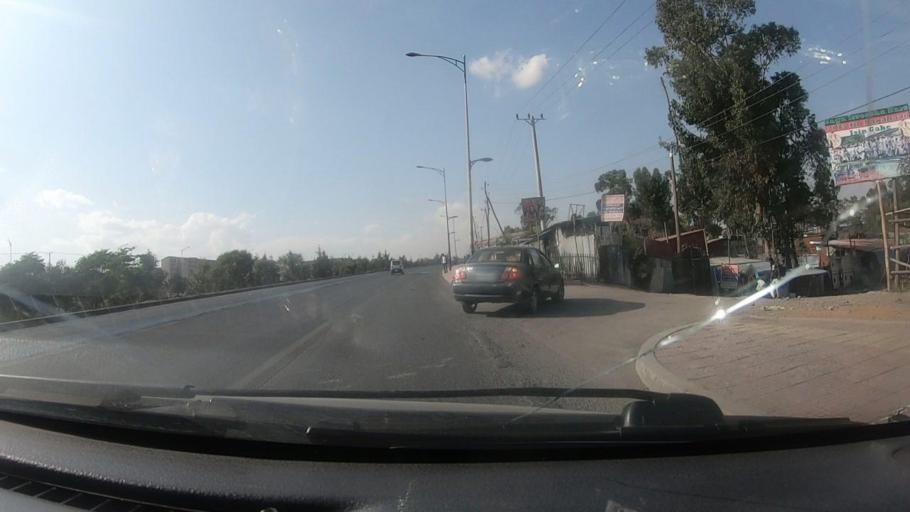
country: ET
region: Adis Abeba
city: Addis Ababa
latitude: 8.9070
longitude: 38.7416
